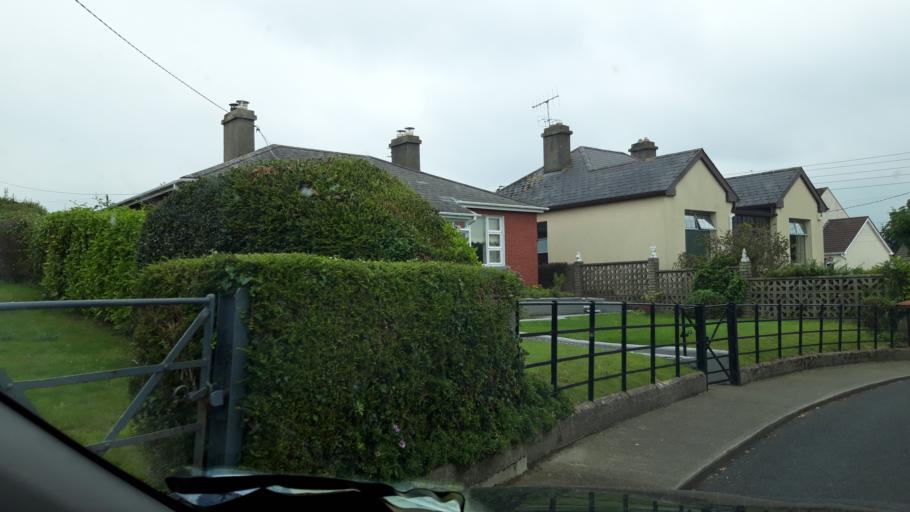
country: IE
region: Munster
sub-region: South Tipperary
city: Cluain Meala
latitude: 52.3580
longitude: -7.6891
